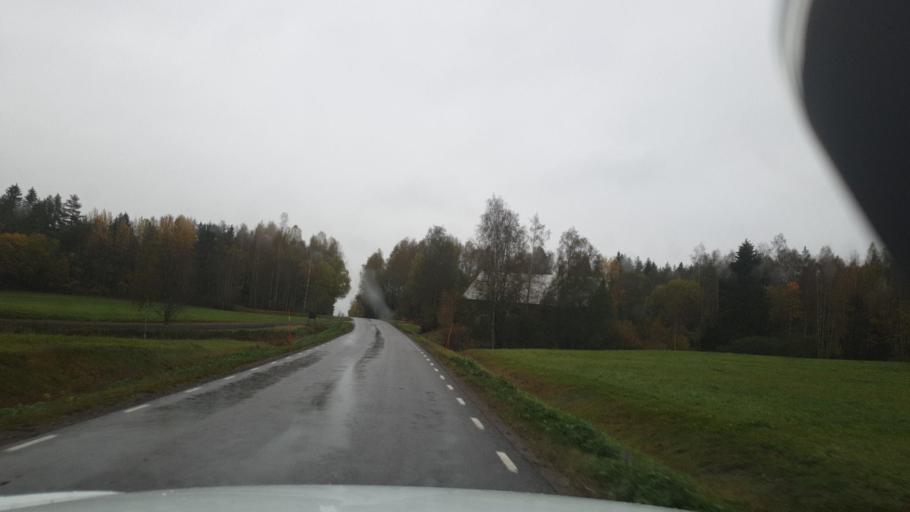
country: SE
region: Vaermland
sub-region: Eda Kommun
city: Charlottenberg
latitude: 59.7919
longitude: 12.1545
